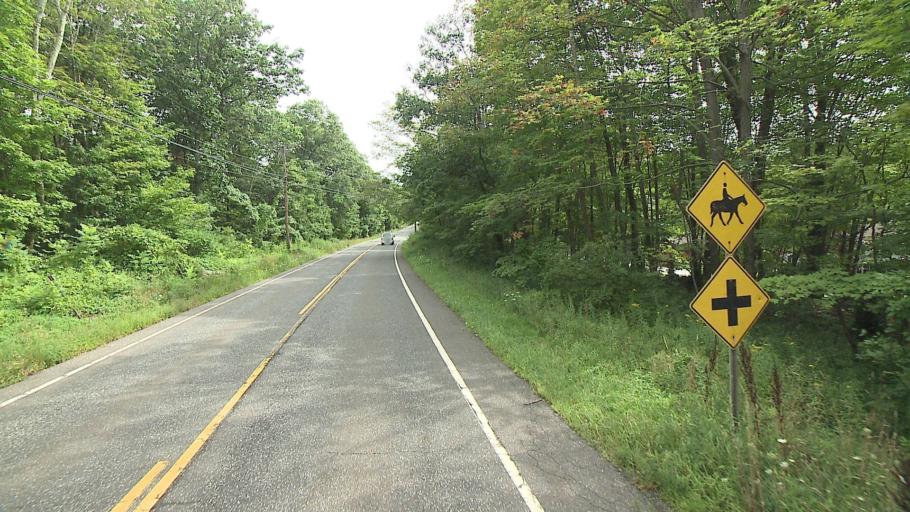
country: US
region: Connecticut
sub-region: Litchfield County
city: Kent
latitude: 41.7336
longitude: -73.4049
